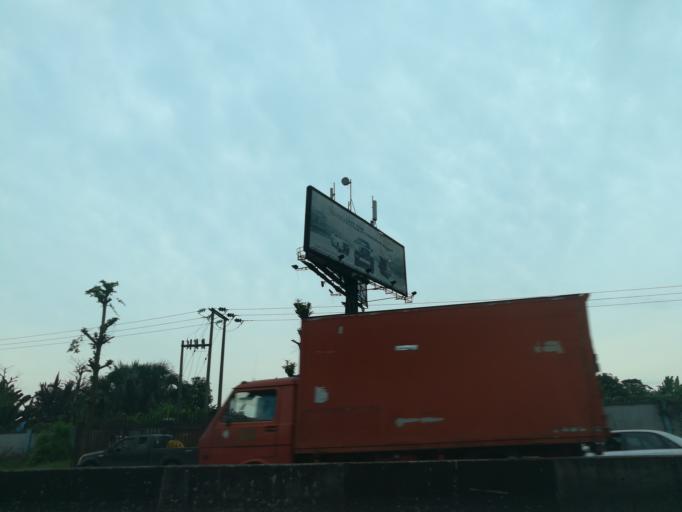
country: NG
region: Rivers
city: Port Harcourt
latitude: 4.8361
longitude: 7.0179
